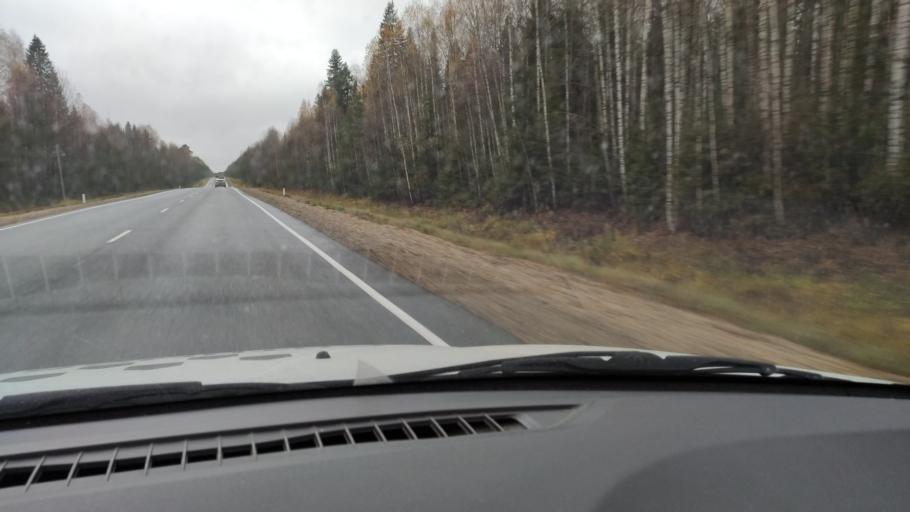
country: RU
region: Kirov
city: Chernaya Kholunitsa
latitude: 58.8590
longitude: 51.6754
